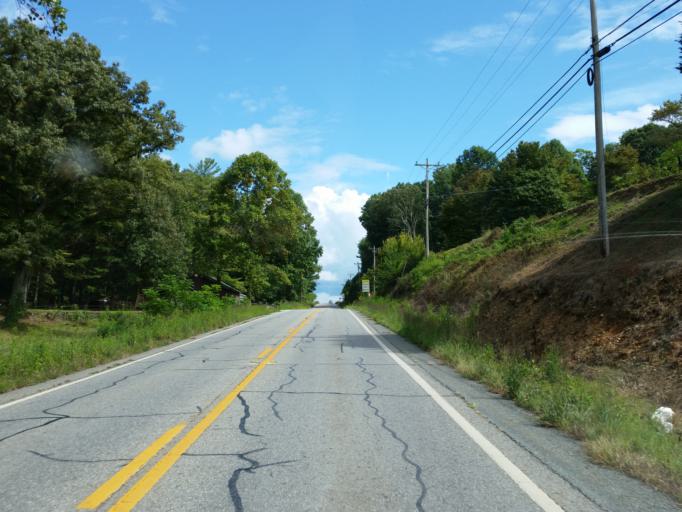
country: US
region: Georgia
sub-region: Fannin County
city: Blue Ridge
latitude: 34.8830
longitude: -84.2526
